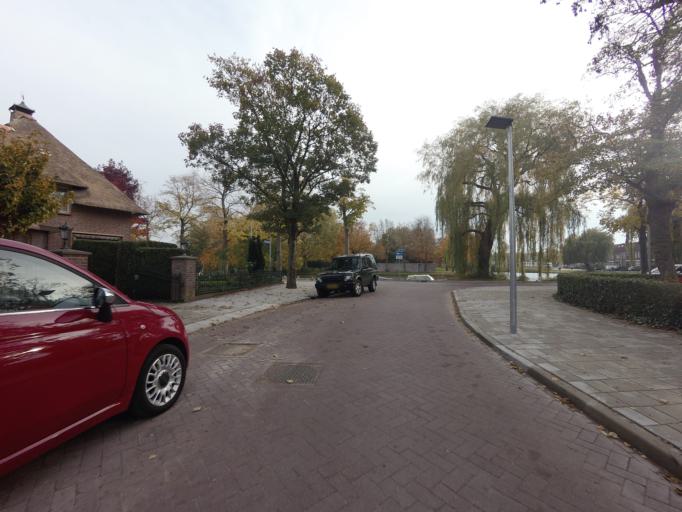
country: NL
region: Utrecht
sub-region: Gemeente Woerden
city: Woerden
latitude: 52.0895
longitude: 4.8810
